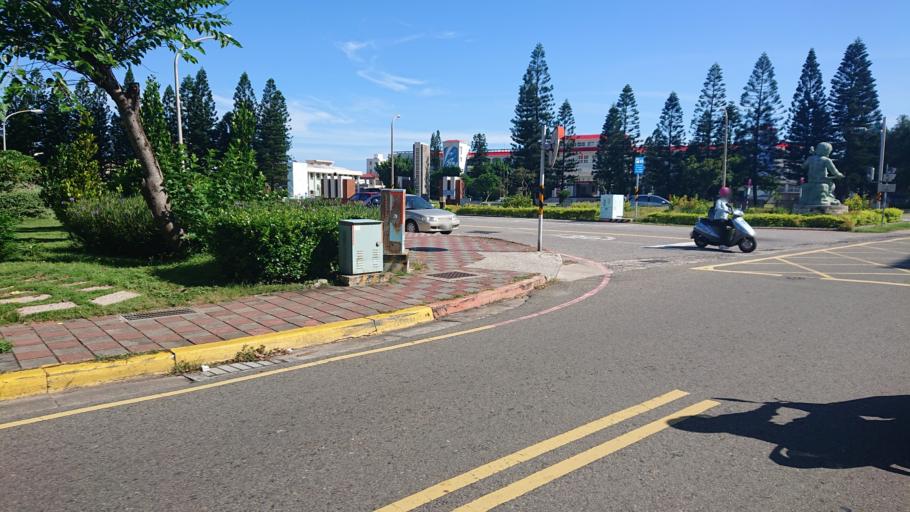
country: TW
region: Taiwan
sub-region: Penghu
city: Ma-kung
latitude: 23.5701
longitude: 119.5692
